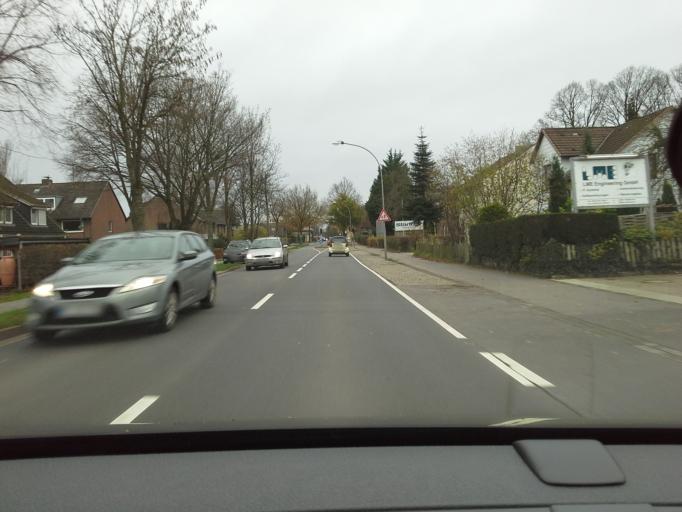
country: DE
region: Schleswig-Holstein
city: Kummerfeld
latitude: 53.6900
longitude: 9.7911
